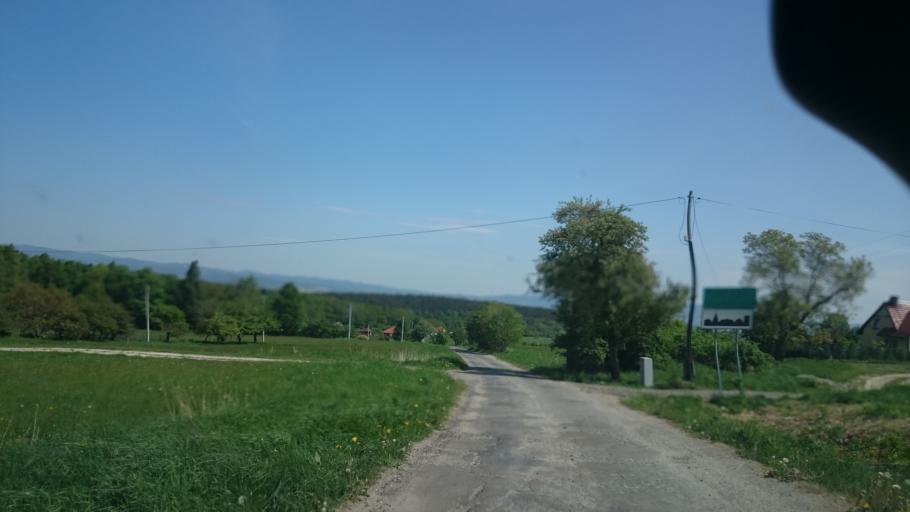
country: PL
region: Lower Silesian Voivodeship
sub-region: Powiat klodzki
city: Polanica-Zdroj
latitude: 50.3623
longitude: 16.5285
